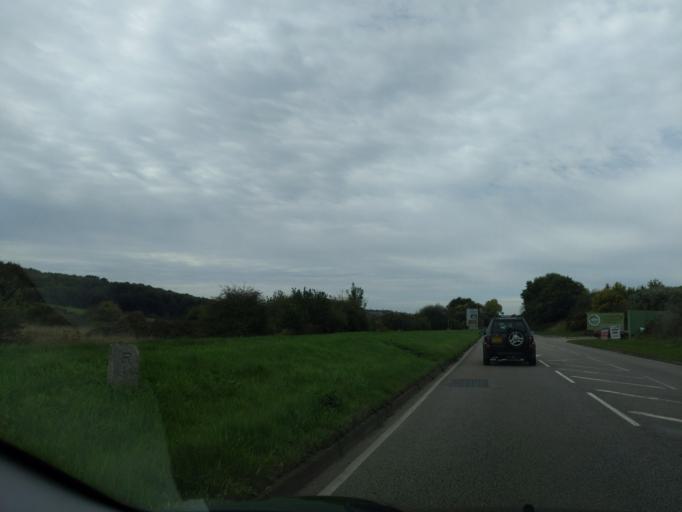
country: GB
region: England
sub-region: Cornwall
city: Wadebridge
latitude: 50.5092
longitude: -4.8110
